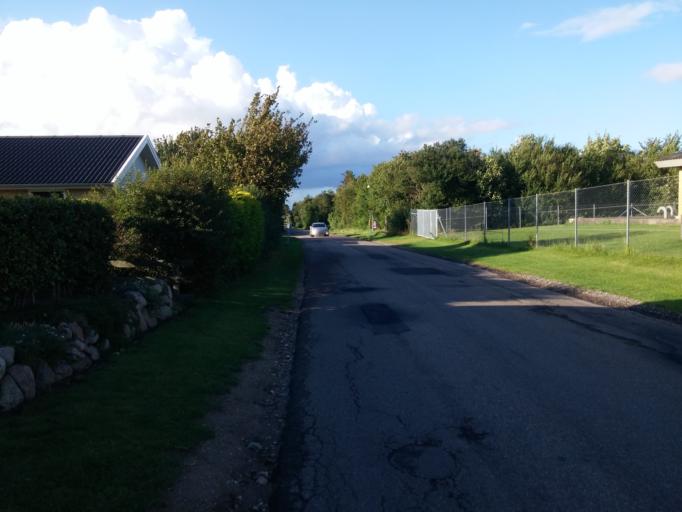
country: DK
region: Zealand
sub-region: Kalundborg Kommune
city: Svebolle
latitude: 55.7511
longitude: 11.3387
